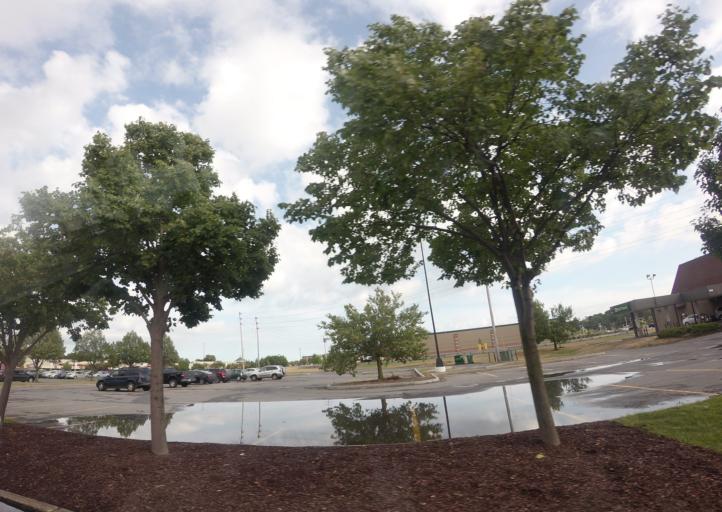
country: US
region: New York
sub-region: Onondaga County
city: East Syracuse
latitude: 43.0467
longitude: -76.0668
